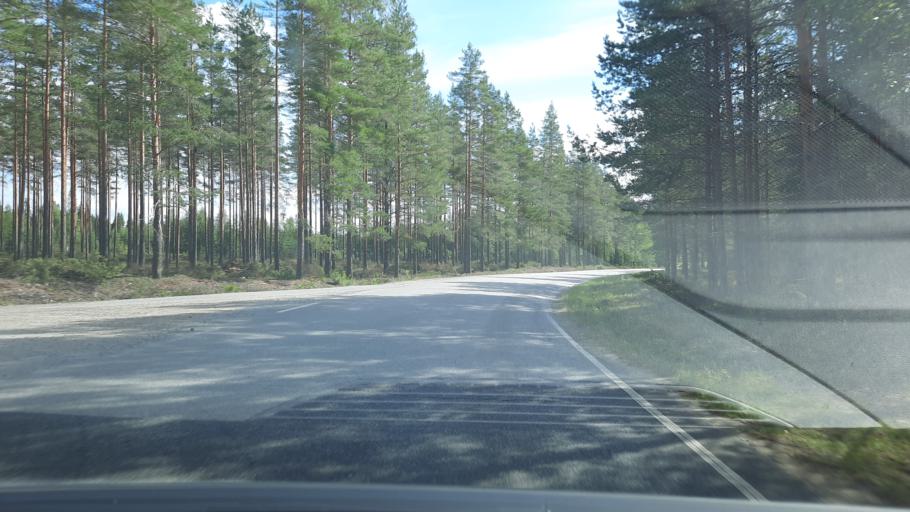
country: FI
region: Pirkanmaa
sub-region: Etelae-Pirkanmaa
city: Urjala
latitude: 61.1704
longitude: 23.3979
